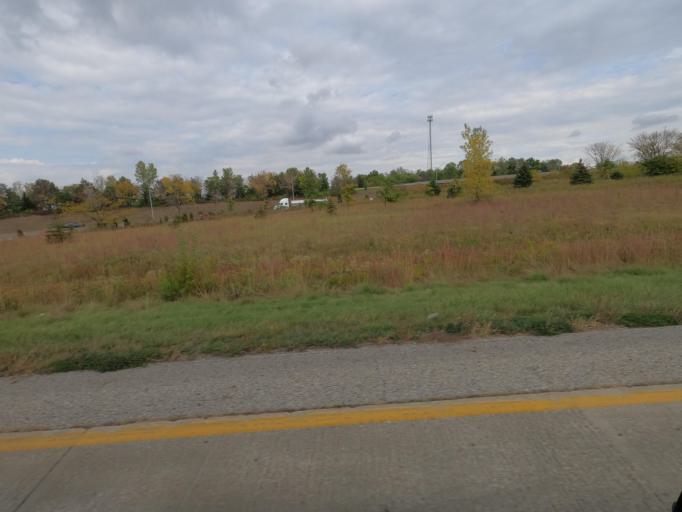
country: US
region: Iowa
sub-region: Polk County
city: Altoona
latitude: 41.6589
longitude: -93.5236
